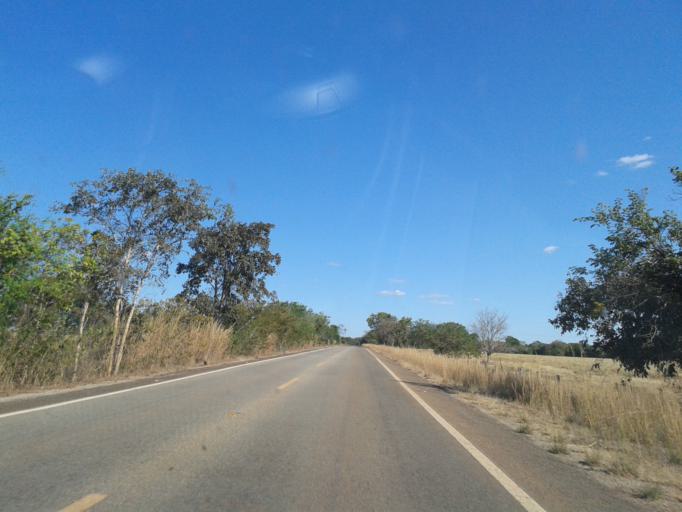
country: BR
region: Goias
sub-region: Mozarlandia
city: Mozarlandia
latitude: -14.2988
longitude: -50.4034
